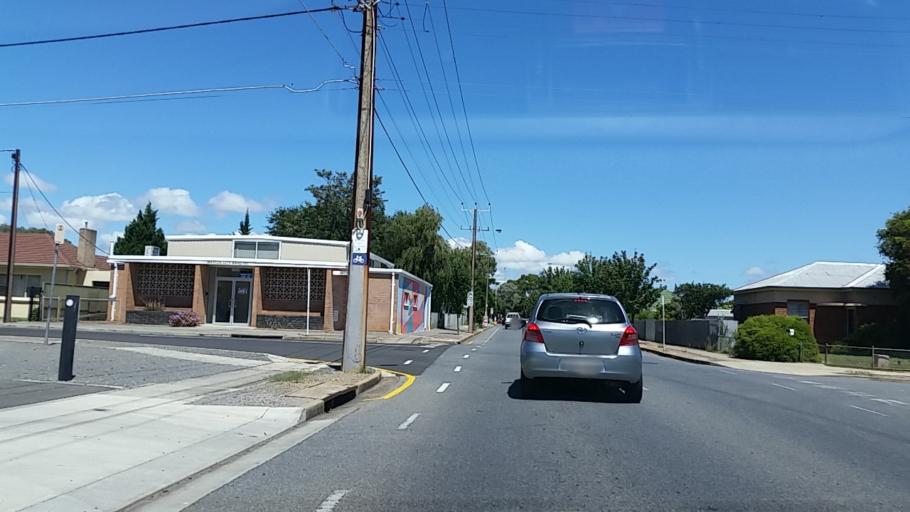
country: AU
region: South Australia
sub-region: Marion
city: South Plympton
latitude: -34.9780
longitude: 138.5647
